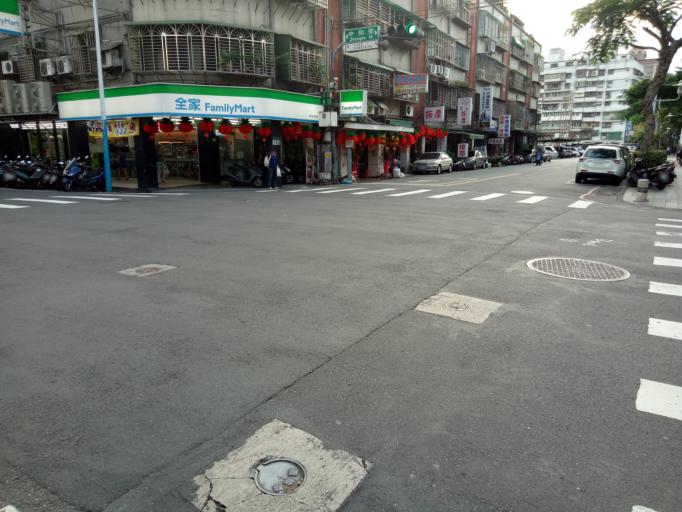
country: TW
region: Taipei
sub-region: Taipei
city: Banqiao
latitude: 25.0451
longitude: 121.4481
